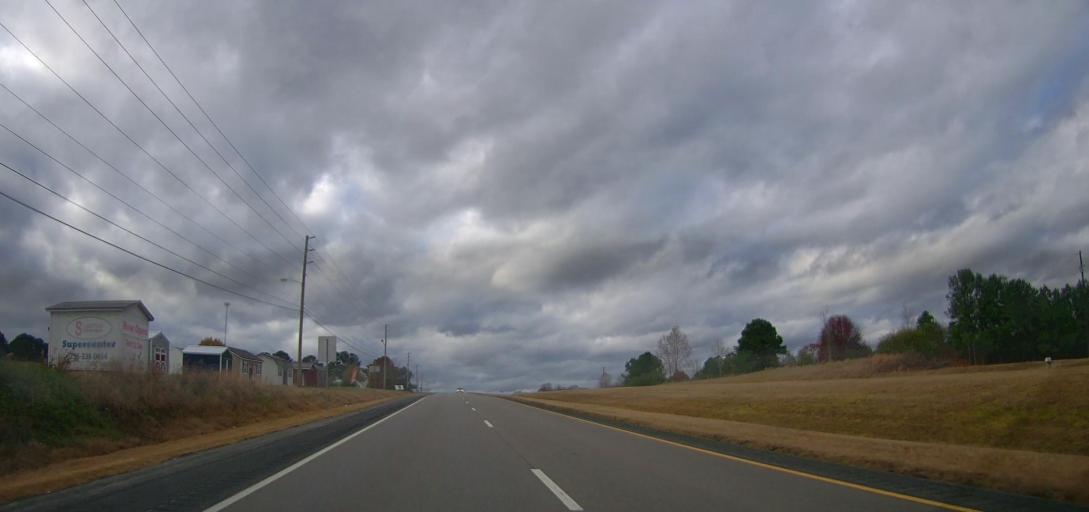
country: US
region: Alabama
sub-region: Morgan County
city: Falkville
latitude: 34.2496
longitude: -86.9676
